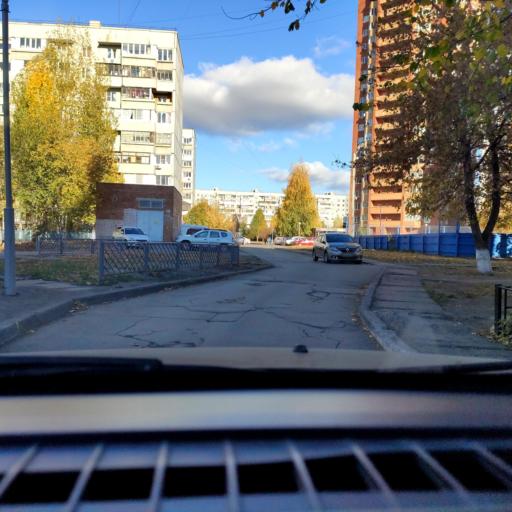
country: RU
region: Samara
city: Tol'yatti
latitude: 53.5442
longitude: 49.3360
